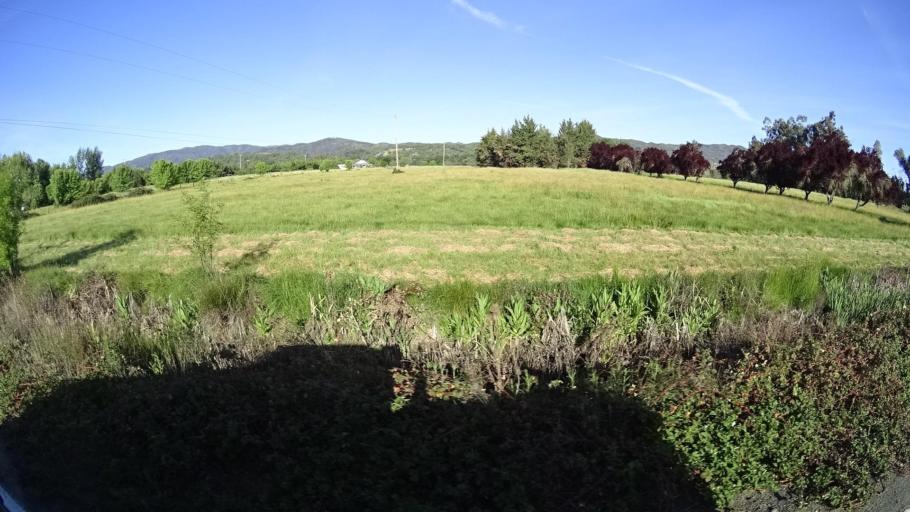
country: US
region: California
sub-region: Lake County
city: North Lakeport
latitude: 39.0842
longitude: -122.9498
